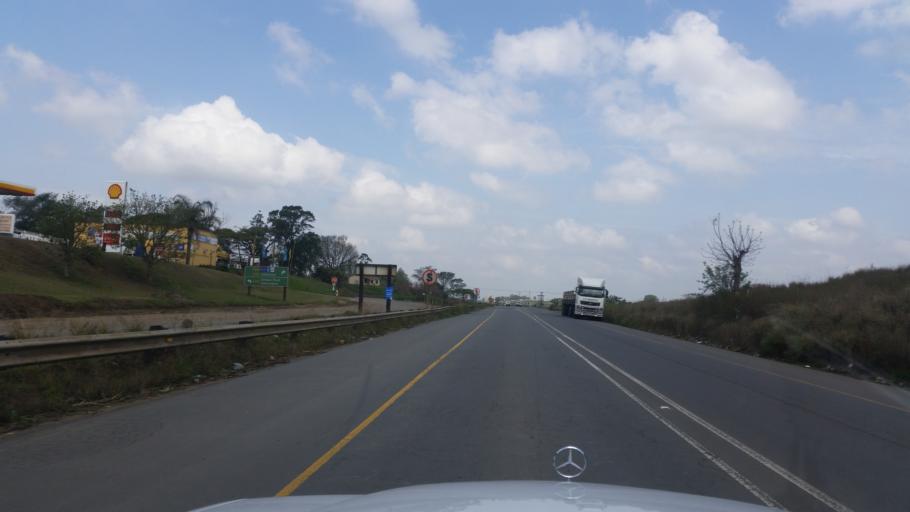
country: ZA
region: KwaZulu-Natal
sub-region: uMgungundlovu District Municipality
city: Camperdown
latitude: -29.7235
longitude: 30.4989
